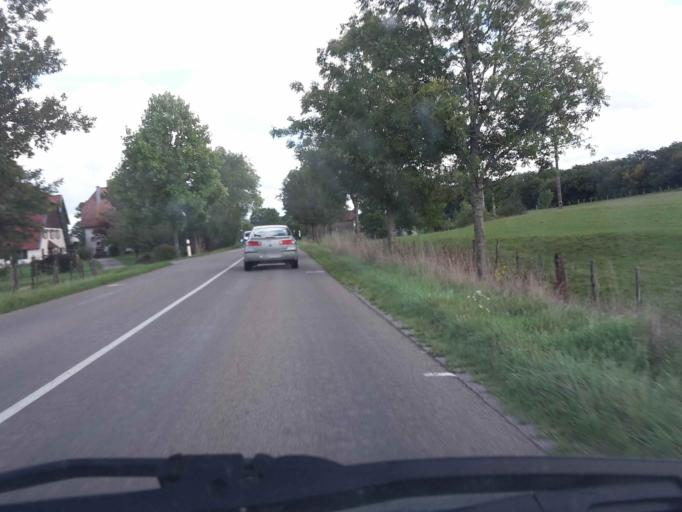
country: FR
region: Franche-Comte
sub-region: Departement du Doubs
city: Saone
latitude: 47.2427
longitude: 6.1459
